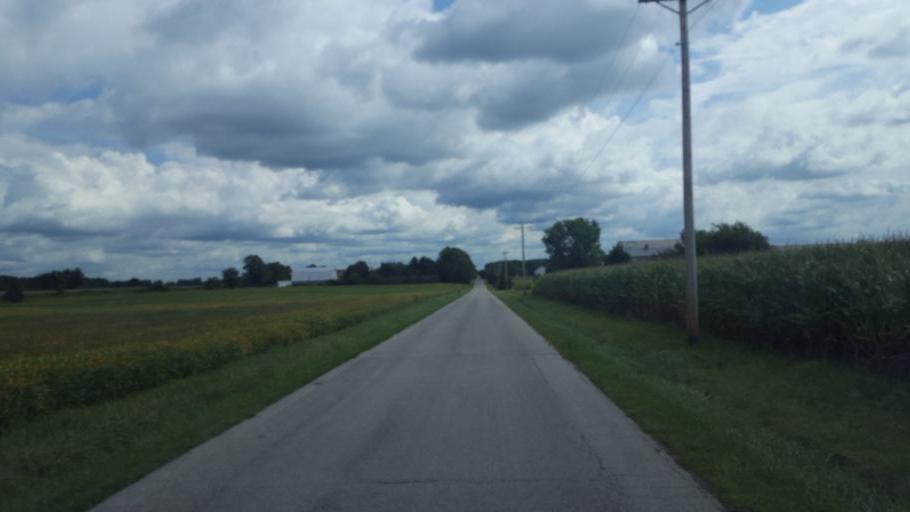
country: US
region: Ohio
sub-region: Sandusky County
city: Mount Carmel
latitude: 41.0956
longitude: -82.9621
